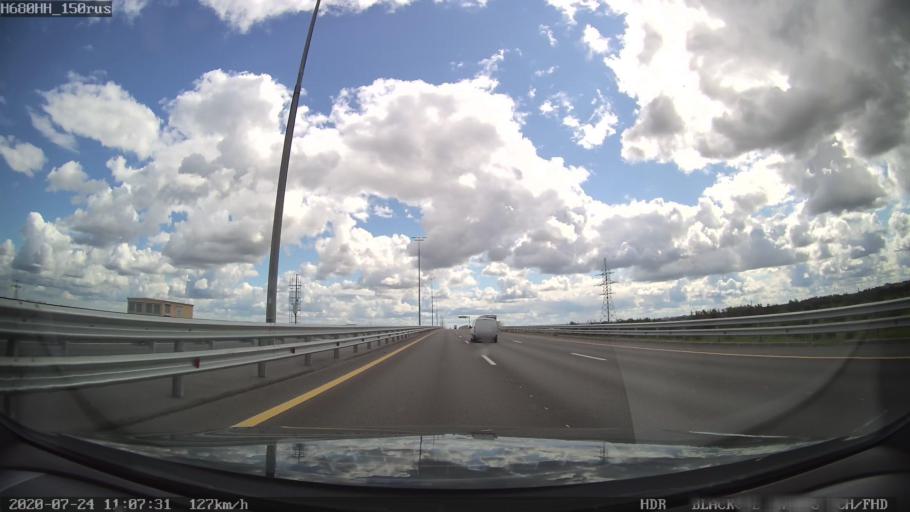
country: RU
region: St.-Petersburg
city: Pushkin
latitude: 59.7560
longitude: 30.4075
